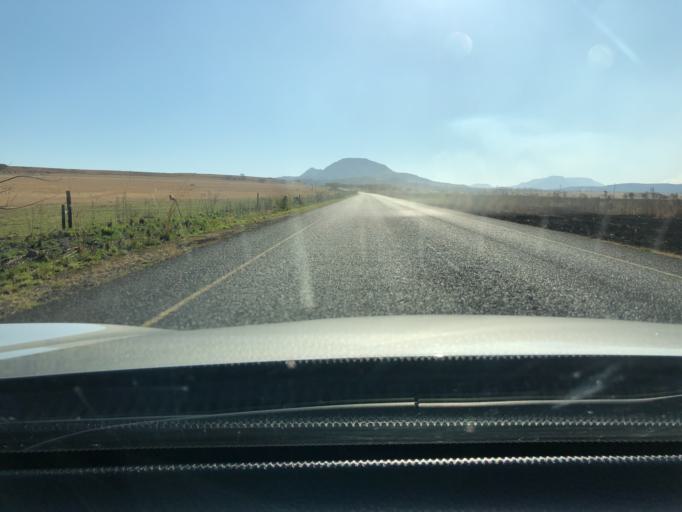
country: ZA
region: KwaZulu-Natal
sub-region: uThukela District Municipality
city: Ekuvukeni
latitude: -28.4047
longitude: 29.9472
